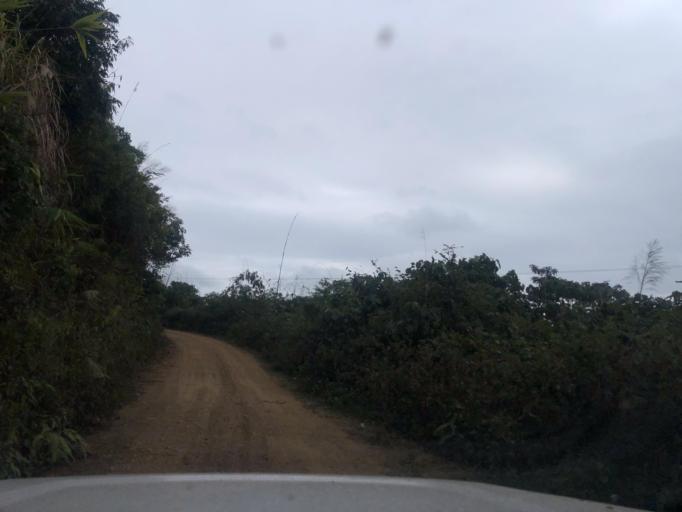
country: LA
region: Phongsali
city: Khoa
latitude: 21.2616
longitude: 102.5887
